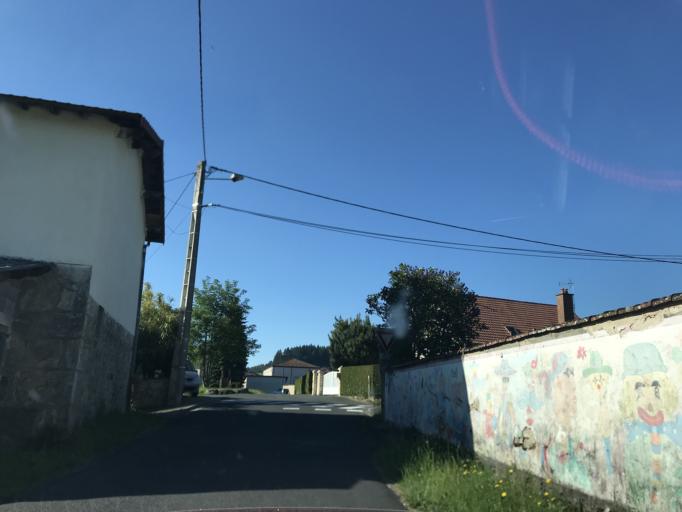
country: FR
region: Auvergne
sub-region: Departement du Puy-de-Dome
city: Job
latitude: 45.6200
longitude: 3.6790
